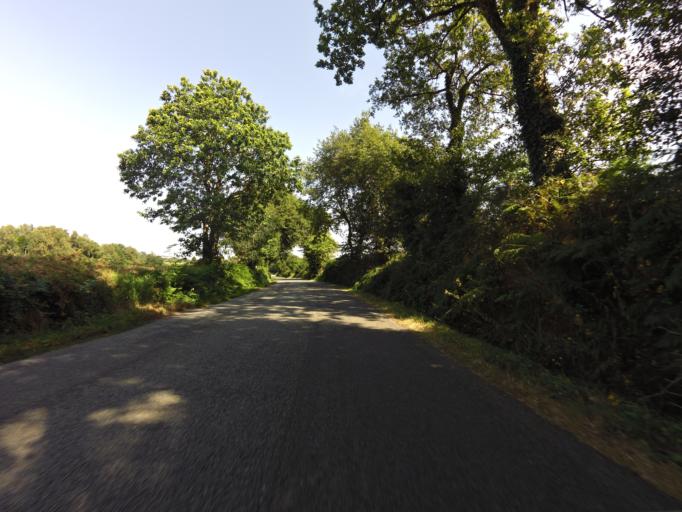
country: FR
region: Brittany
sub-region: Departement du Morbihan
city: Questembert
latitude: 47.6599
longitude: -2.4340
